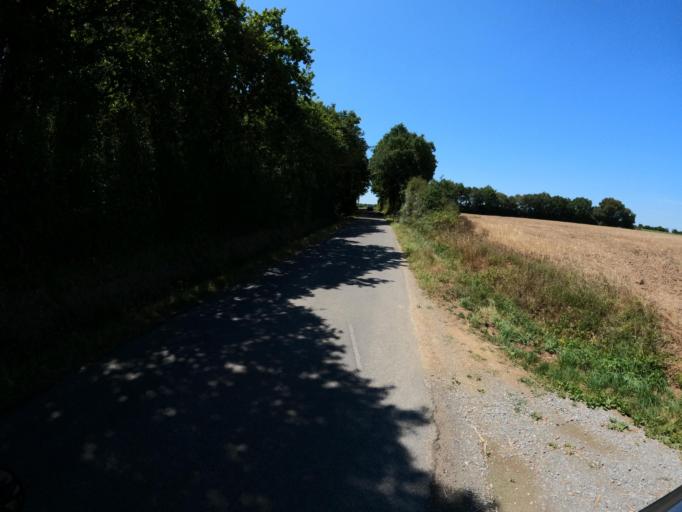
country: FR
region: Pays de la Loire
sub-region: Departement de la Loire-Atlantique
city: Lege
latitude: 46.9386
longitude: -1.6285
